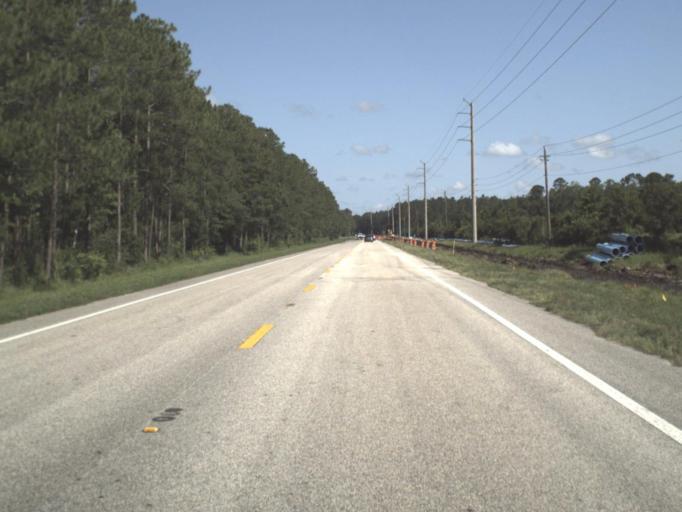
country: US
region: Florida
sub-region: Saint Johns County
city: Saint Augustine
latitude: 29.9420
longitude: -81.4402
